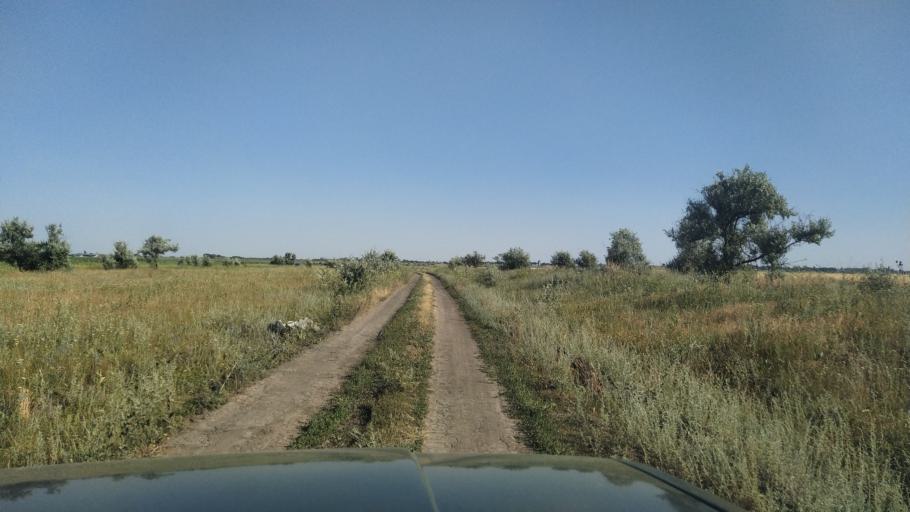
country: RU
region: Rostov
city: Kuleshovka
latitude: 47.1300
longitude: 39.6440
